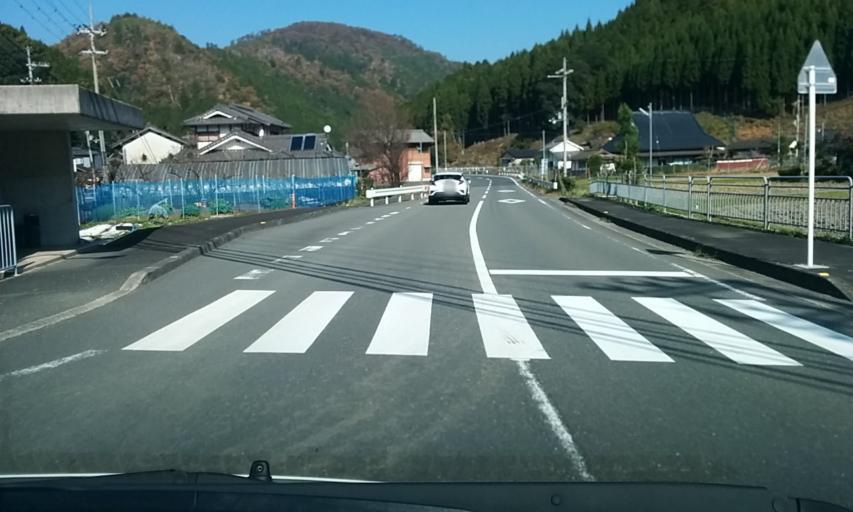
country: JP
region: Kyoto
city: Kameoka
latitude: 35.1945
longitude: 135.5213
